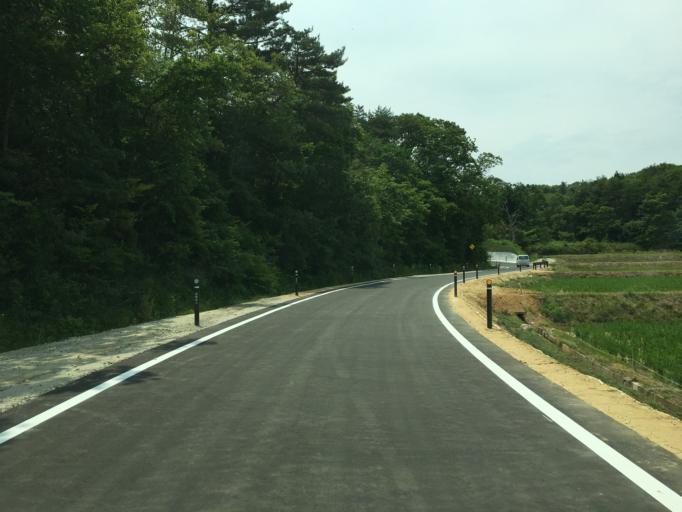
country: JP
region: Miyagi
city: Marumori
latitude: 37.7580
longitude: 140.9742
